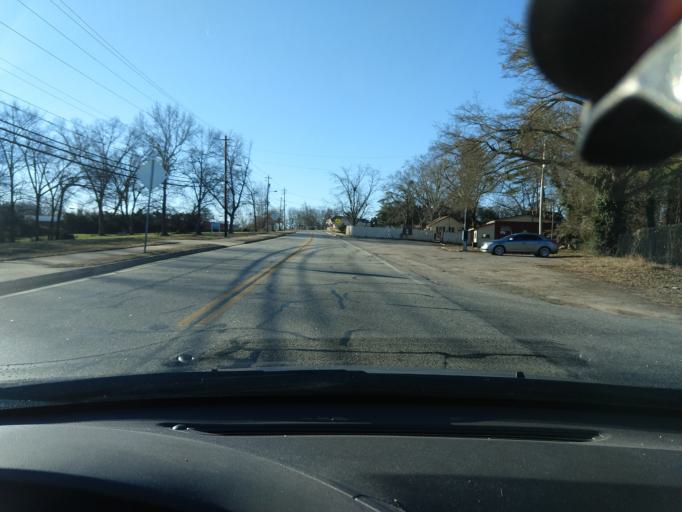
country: US
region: Georgia
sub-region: Jackson County
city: Commerce
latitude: 34.2108
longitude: -83.4624
